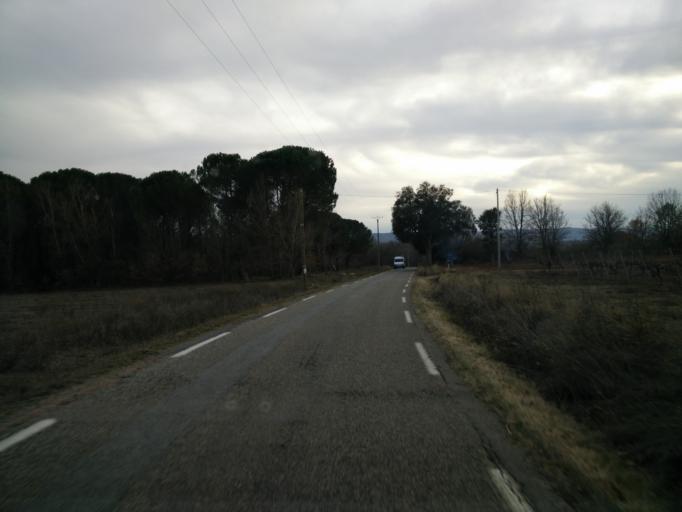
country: FR
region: Provence-Alpes-Cote d'Azur
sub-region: Departement du Var
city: Vidauban
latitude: 43.3844
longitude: 6.4419
